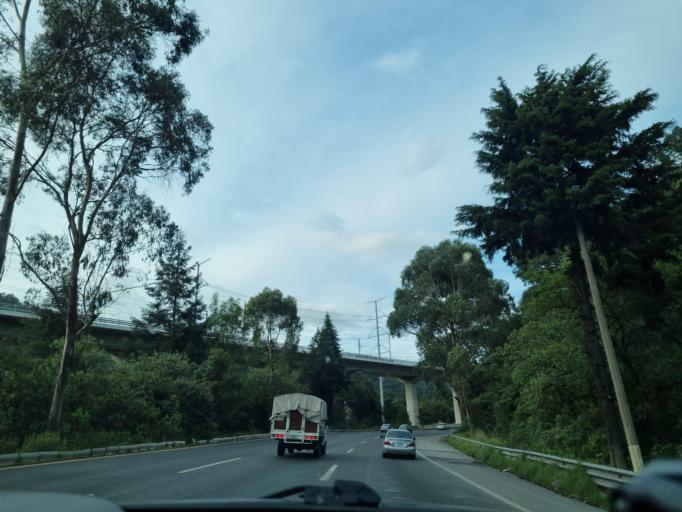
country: MX
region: Morelos
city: San Jeronimo Acazulco
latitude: 19.2950
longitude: -99.4167
